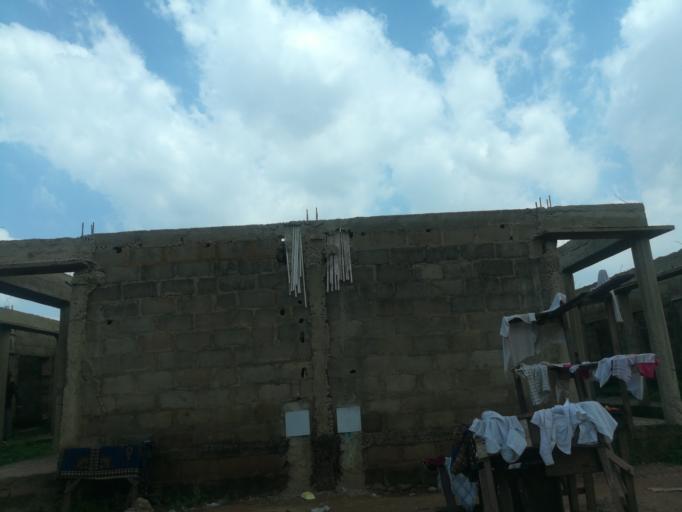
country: NG
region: Oyo
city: Ibadan
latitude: 7.3881
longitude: 3.8839
